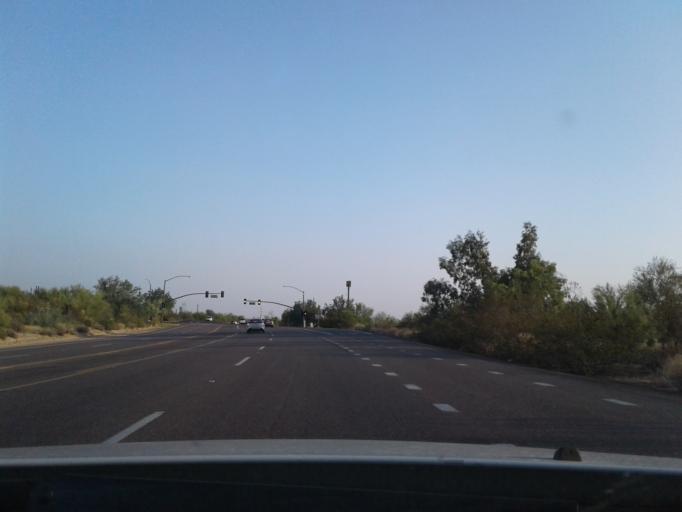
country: US
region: Arizona
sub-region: Maricopa County
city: Carefree
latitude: 33.7282
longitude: -111.9260
